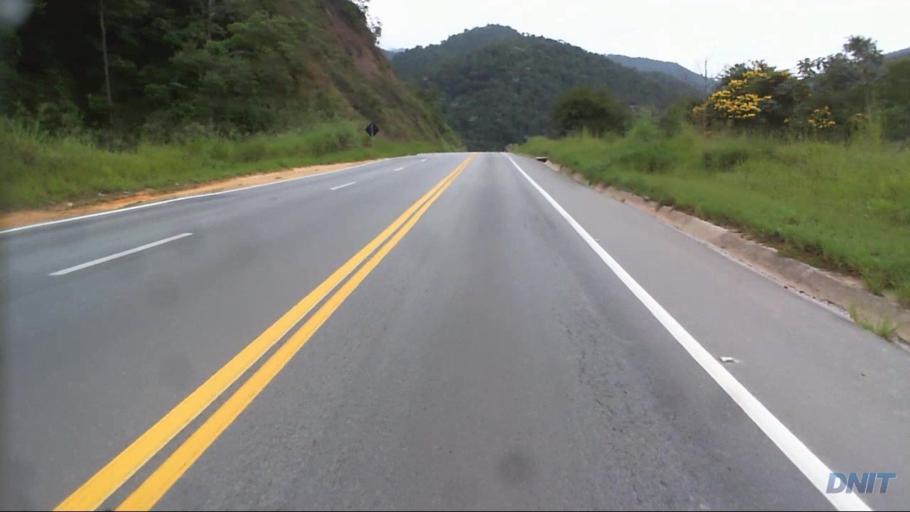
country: BR
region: Minas Gerais
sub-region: Nova Era
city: Nova Era
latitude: -19.6431
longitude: -42.9123
